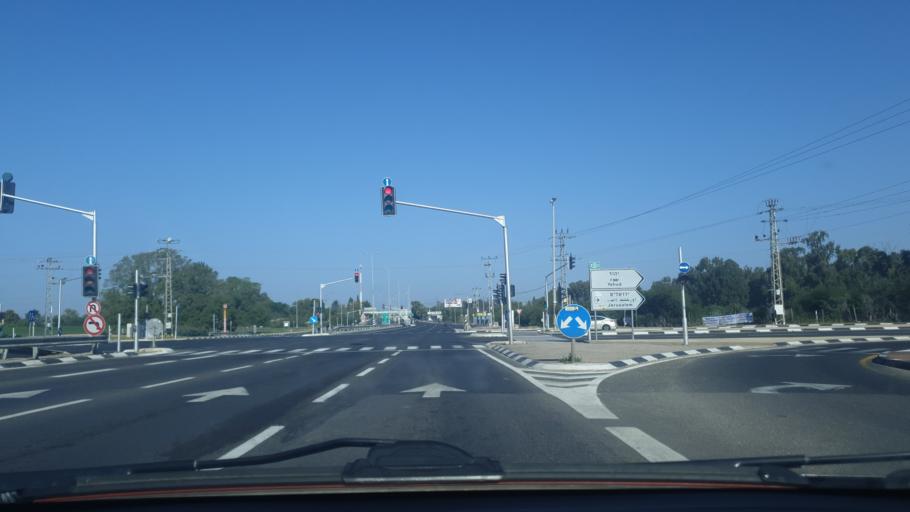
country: IL
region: Central District
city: Bet Dagan
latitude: 32.0008
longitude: 34.8216
